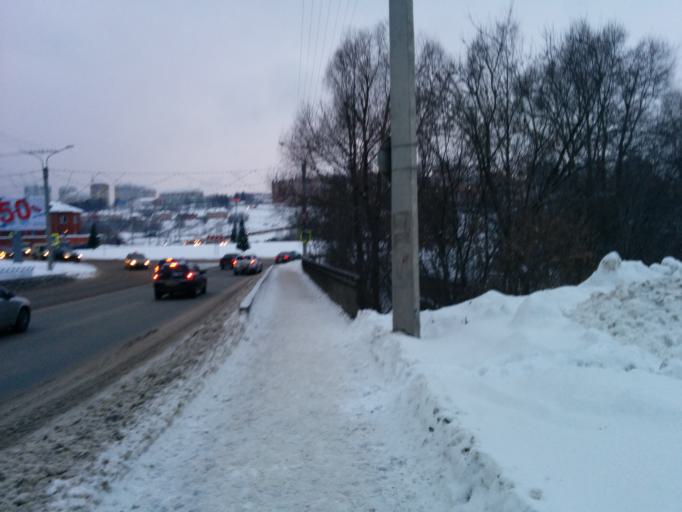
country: RU
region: Chuvashia
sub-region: Cheboksarskiy Rayon
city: Cheboksary
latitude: 56.1362
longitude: 47.2382
